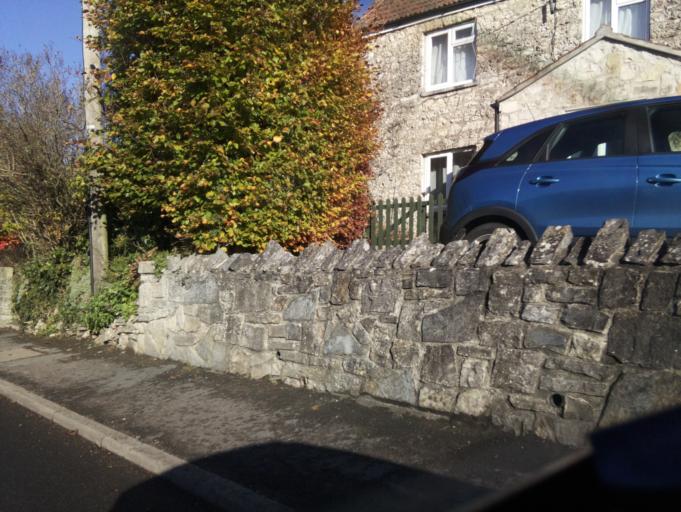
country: GB
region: England
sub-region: Somerset
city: Langport
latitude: 51.0360
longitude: -2.8135
